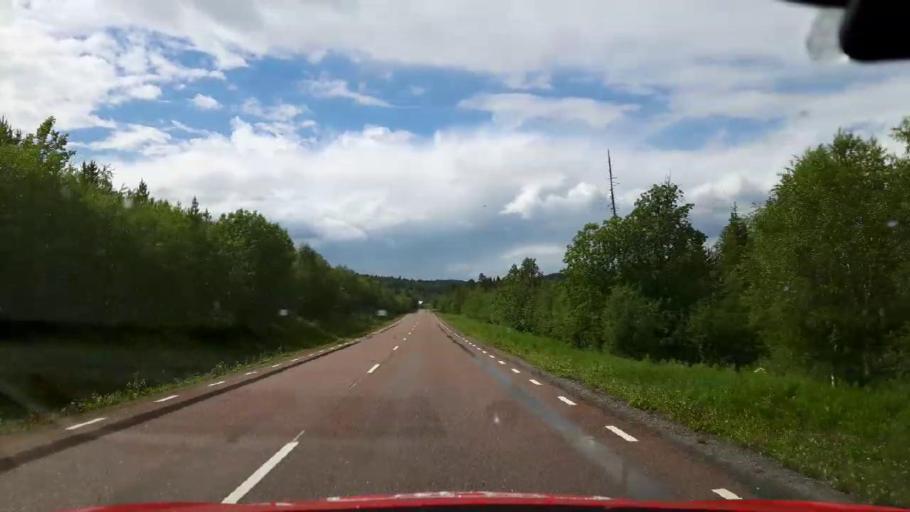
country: SE
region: Jaemtland
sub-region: Krokoms Kommun
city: Valla
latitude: 63.9007
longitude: 14.2344
